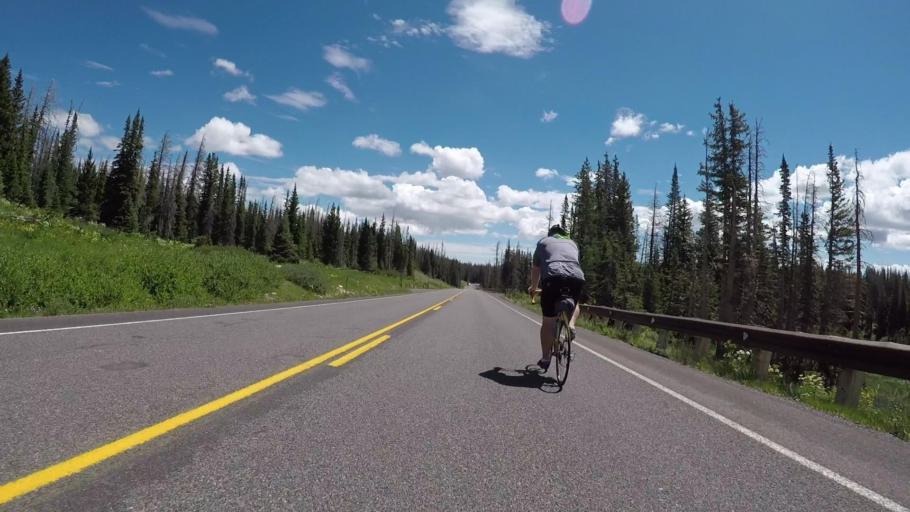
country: US
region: Wyoming
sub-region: Carbon County
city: Saratoga
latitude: 41.3515
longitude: -106.2712
